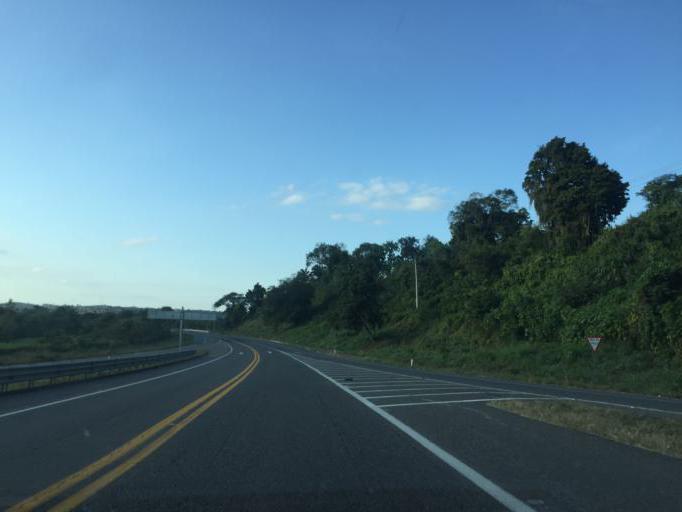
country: MX
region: Veracruz
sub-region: Papantla
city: Residencial Tajin
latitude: 20.6243
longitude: -97.3912
